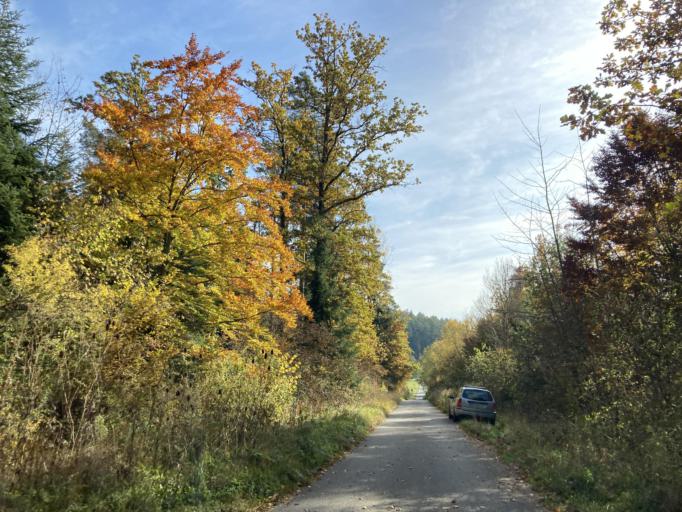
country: DE
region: Baden-Wuerttemberg
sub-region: Tuebingen Region
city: Bodelshausen
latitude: 48.4065
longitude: 8.9653
